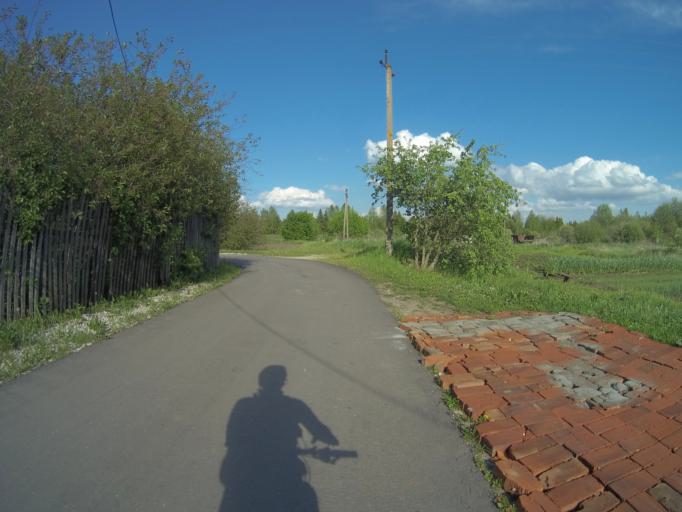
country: RU
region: Vladimir
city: Suzdal'
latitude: 56.4050
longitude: 40.4681
